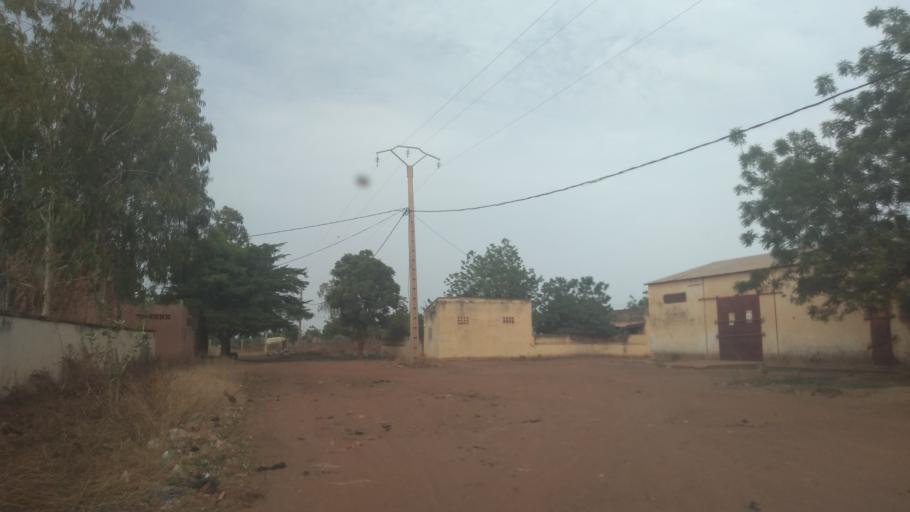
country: ML
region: Bamako
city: Bamako
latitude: 12.6184
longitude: -7.7785
